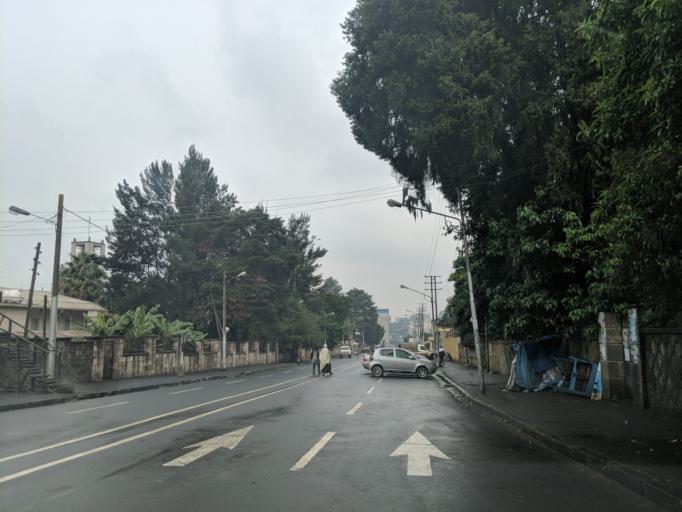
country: ET
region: Adis Abeba
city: Addis Ababa
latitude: 9.0309
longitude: 38.7655
